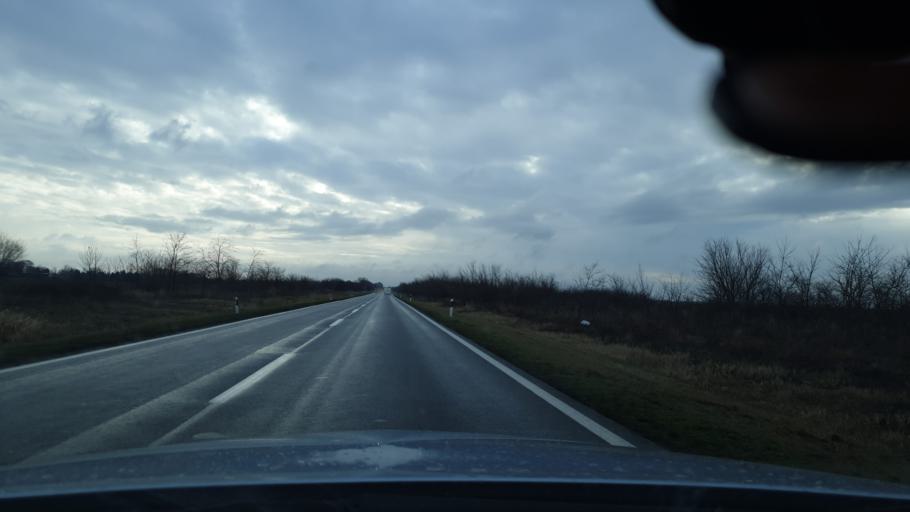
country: RS
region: Autonomna Pokrajina Vojvodina
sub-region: Juznobanatski Okrug
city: Kovin
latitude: 44.7707
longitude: 20.9445
